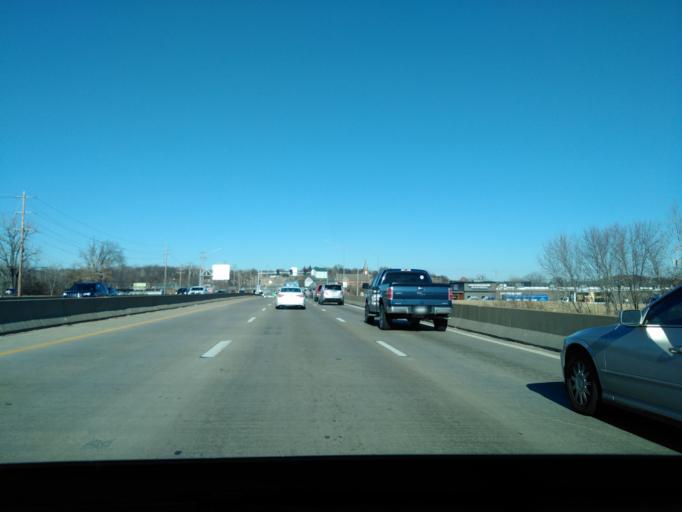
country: US
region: Missouri
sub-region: Saint Louis County
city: Valley Park
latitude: 38.5465
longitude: -90.4945
